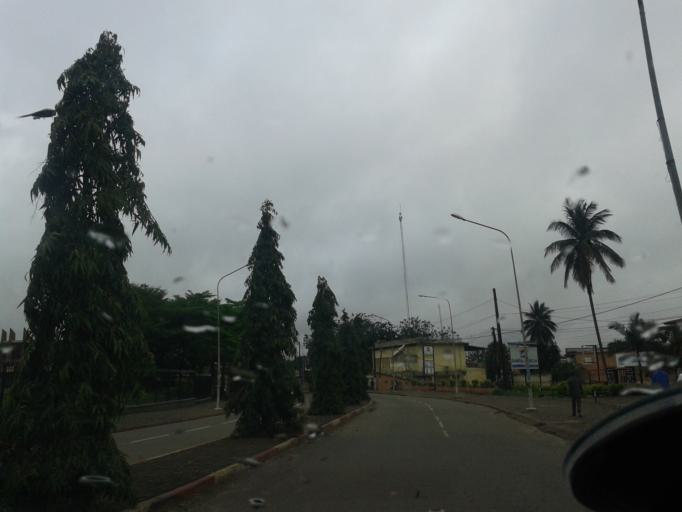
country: CM
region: Centre
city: Yaounde
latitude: 3.8736
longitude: 11.5175
